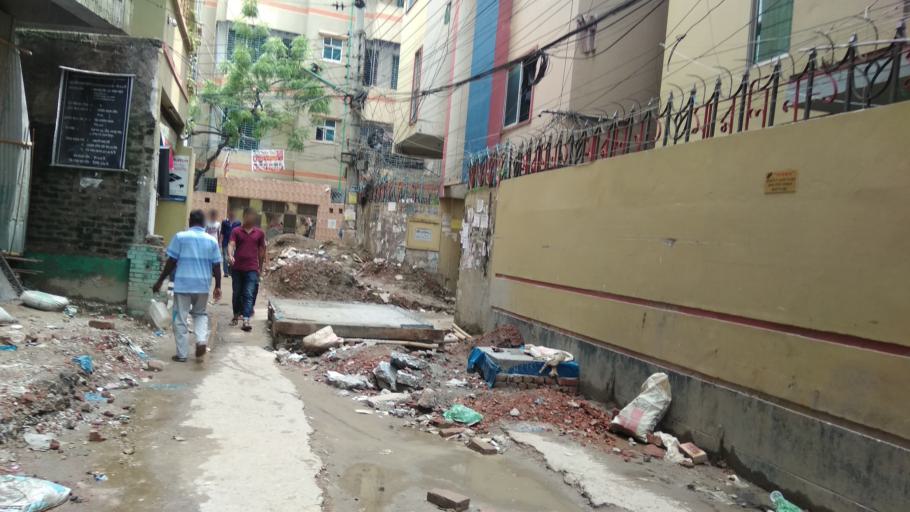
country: BD
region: Dhaka
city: Azimpur
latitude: 23.8040
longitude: 90.3656
